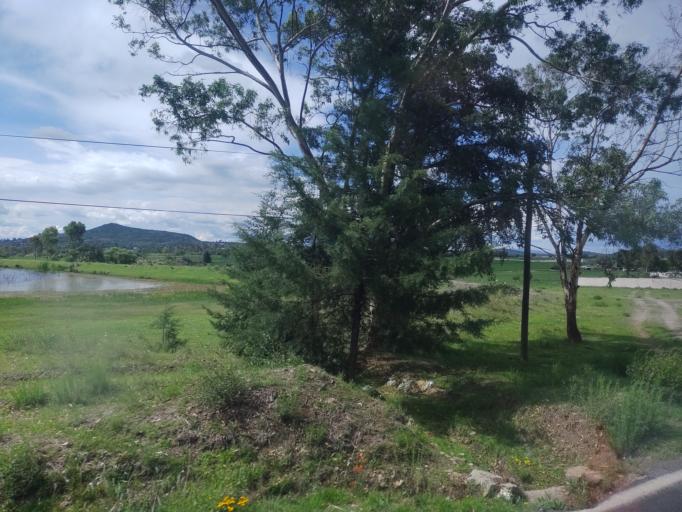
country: MX
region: Mexico
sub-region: Aculco
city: El Colorado
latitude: 20.0965
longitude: -99.7497
